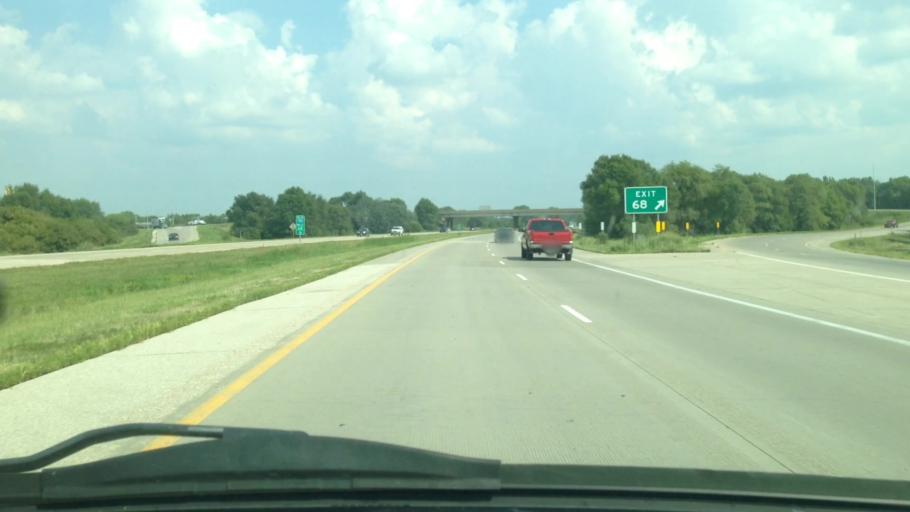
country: US
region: Iowa
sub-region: Black Hawk County
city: Elk Run Heights
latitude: 42.4592
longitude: -92.2583
